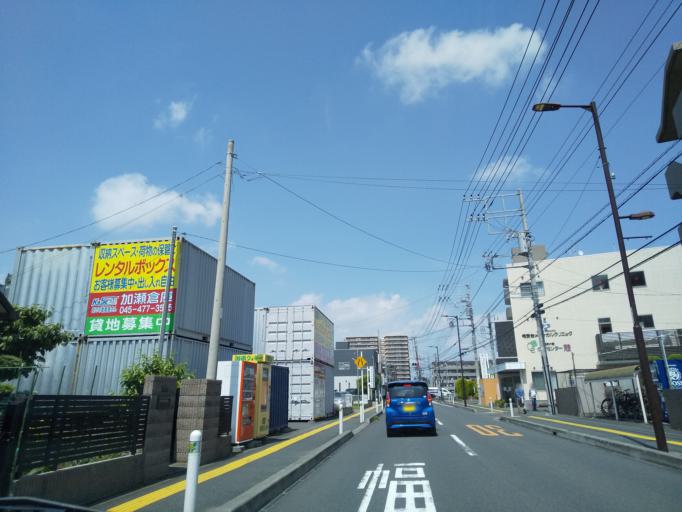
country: JP
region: Kanagawa
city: Zama
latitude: 35.5009
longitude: 139.4123
